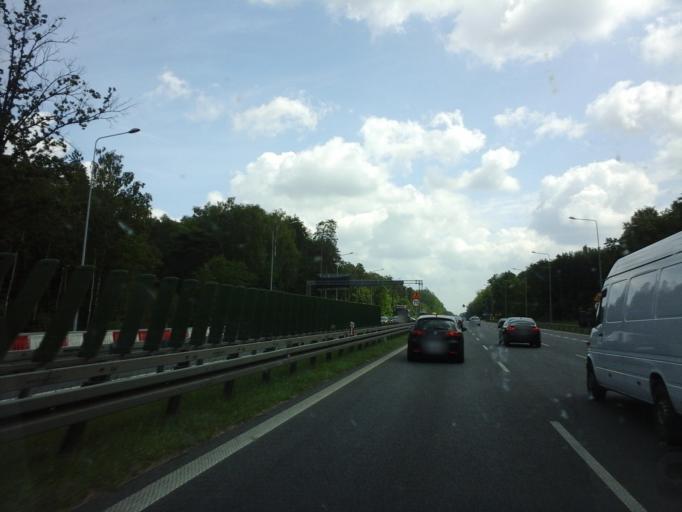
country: PL
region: Lodz Voivodeship
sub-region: Powiat lodzki wschodni
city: Rzgow
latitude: 51.6357
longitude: 19.5021
